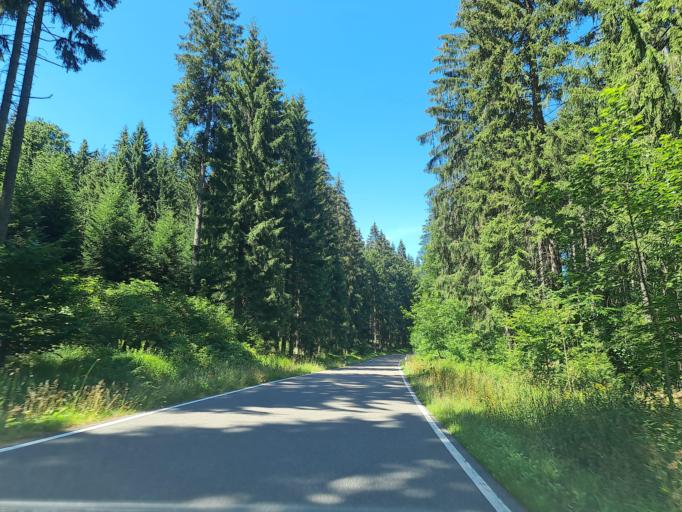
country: DE
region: Saxony
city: Rechenberg-Bienenmuhle
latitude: 50.7108
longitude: 13.5419
